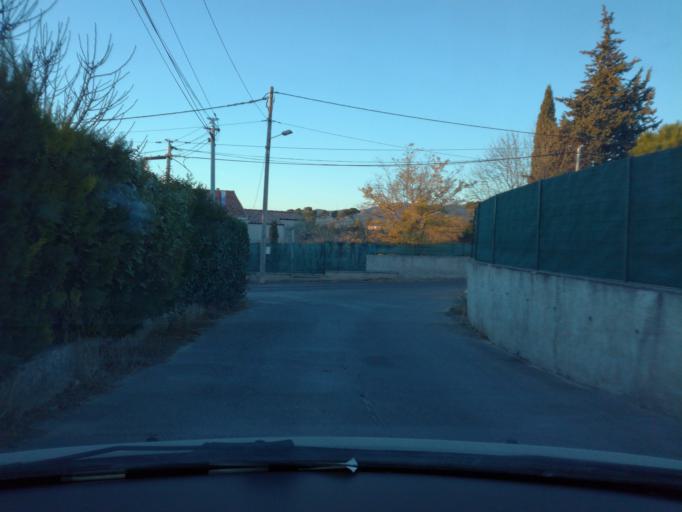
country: FR
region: Provence-Alpes-Cote d'Azur
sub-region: Departement des Bouches-du-Rhone
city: Plan-de-Cuques
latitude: 43.3310
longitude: 5.4611
